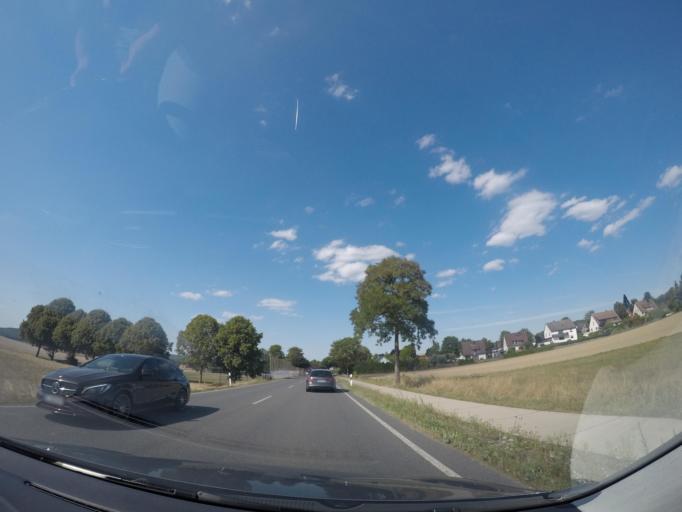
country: DE
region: Lower Saxony
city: Seesen
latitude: 51.8618
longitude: 10.1792
